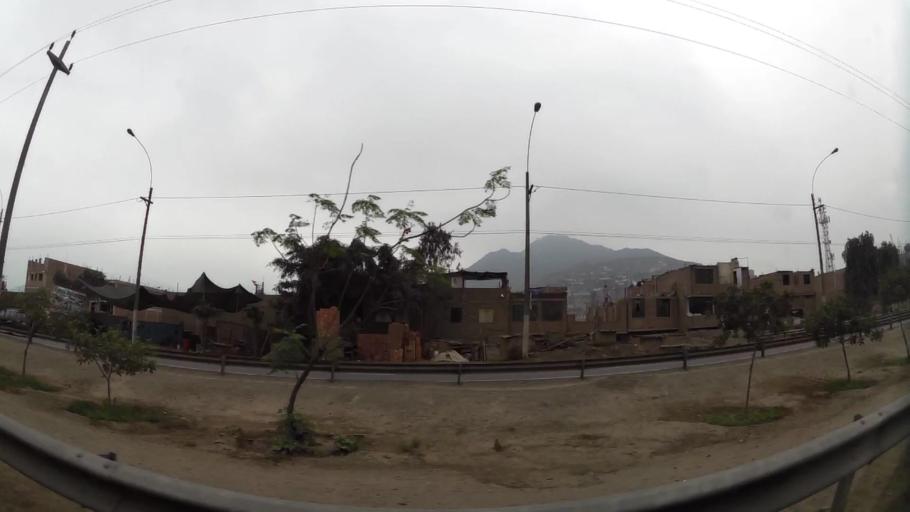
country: PE
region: Lima
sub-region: Lima
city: Vitarte
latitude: -12.0209
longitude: -76.9542
